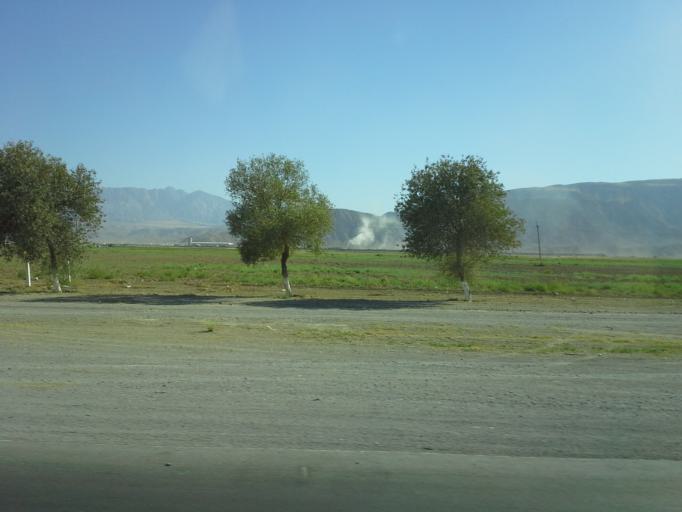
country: TM
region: Ahal
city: Abadan
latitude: 38.1694
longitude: 57.9203
